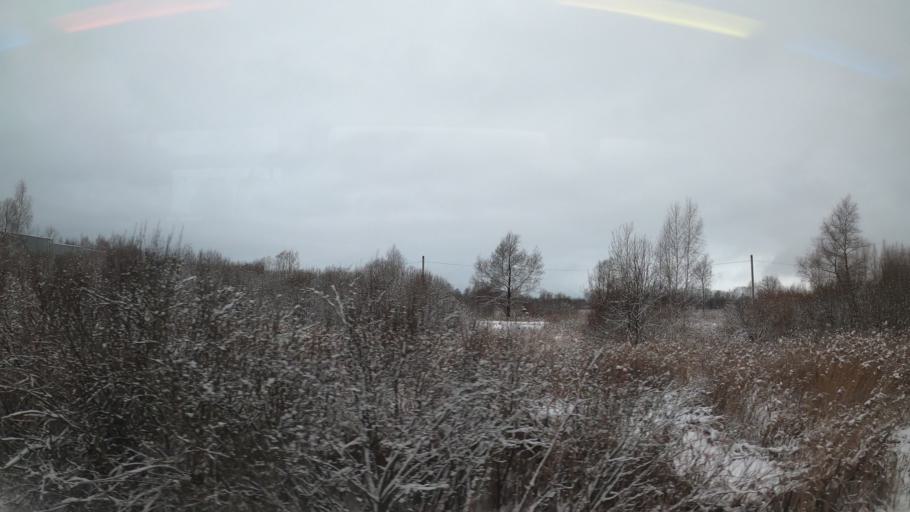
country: RU
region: Jaroslavl
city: Pereslavl'-Zalesskiy
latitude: 56.7257
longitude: 38.9042
